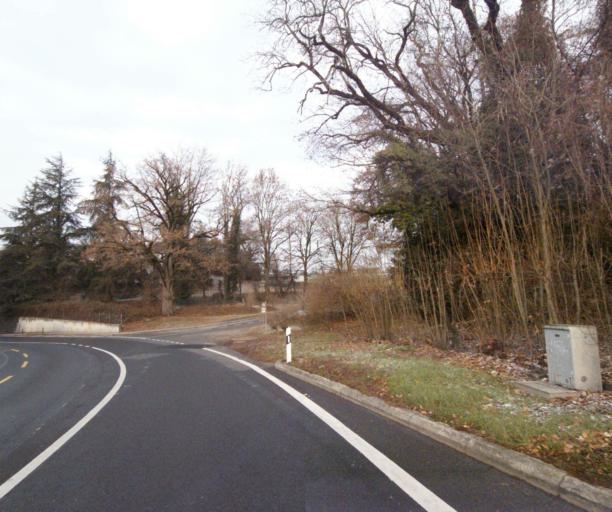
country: CH
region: Vaud
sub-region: Riviera-Pays-d'Enhaut District
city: Le Chatelard
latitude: 46.4515
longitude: 6.8806
